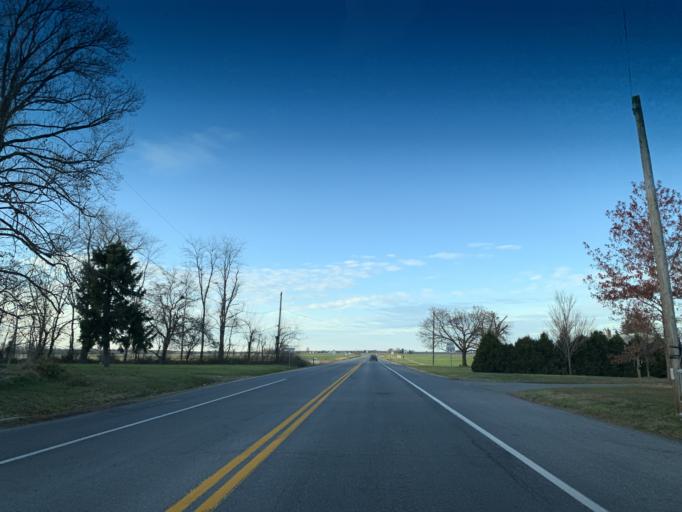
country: US
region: Maryland
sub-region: Kent County
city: Chestertown
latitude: 39.2399
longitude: -76.0672
